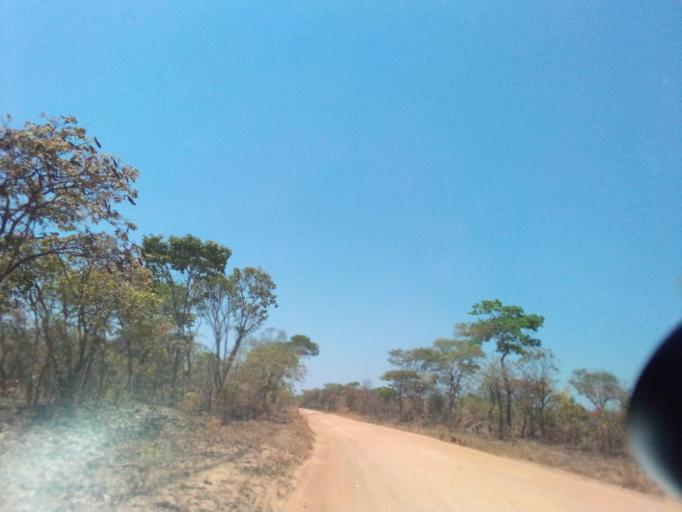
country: ZM
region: Northern
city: Mpika
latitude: -12.2482
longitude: 30.6681
